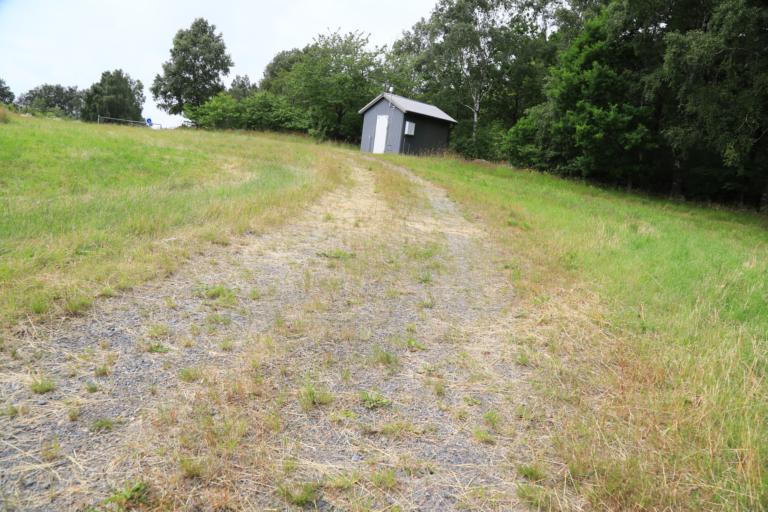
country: SE
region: Halland
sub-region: Varbergs Kommun
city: Traslovslage
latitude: 57.1008
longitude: 12.2985
